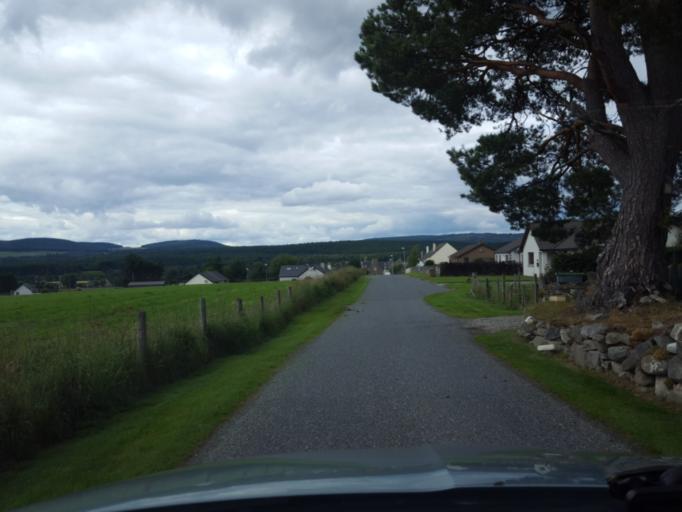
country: GB
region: Scotland
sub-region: Highland
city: Grantown on Spey
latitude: 57.3361
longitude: -3.5349
